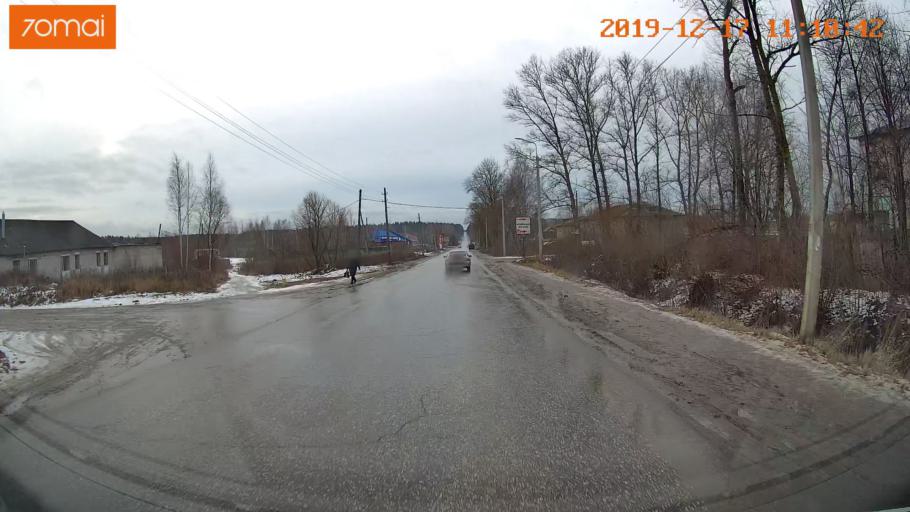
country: RU
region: Vladimir
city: Gus'-Khrustal'nyy
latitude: 55.5911
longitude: 40.6402
